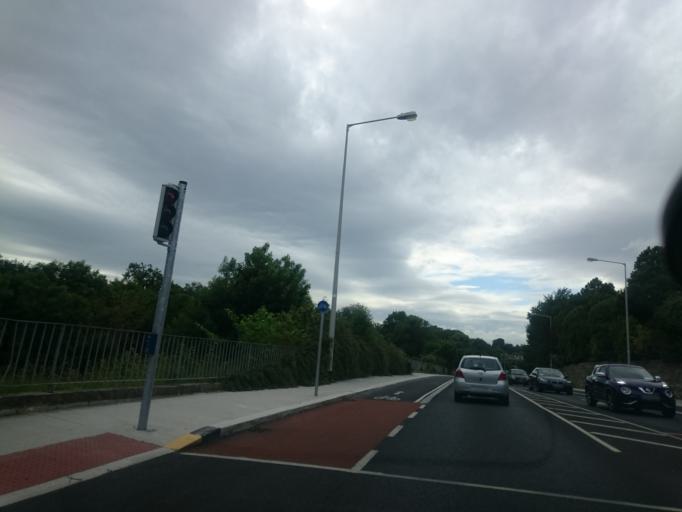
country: IE
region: Leinster
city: Rathgar
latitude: 53.3025
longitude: -6.2675
